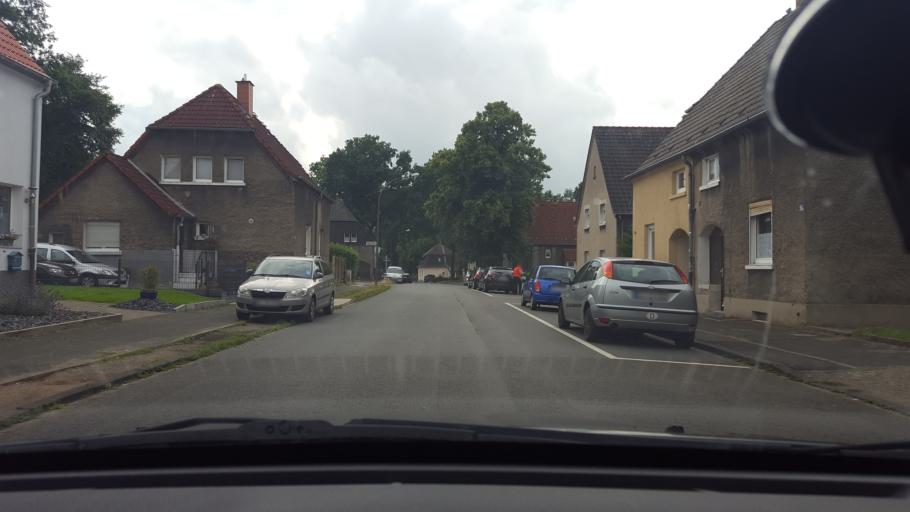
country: DE
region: North Rhine-Westphalia
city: Marl
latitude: 51.6120
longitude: 7.0780
